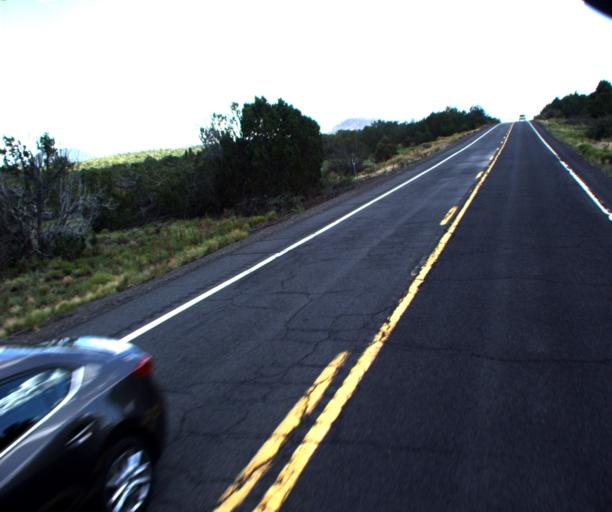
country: US
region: Arizona
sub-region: Coconino County
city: Williams
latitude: 35.4379
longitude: -112.1714
